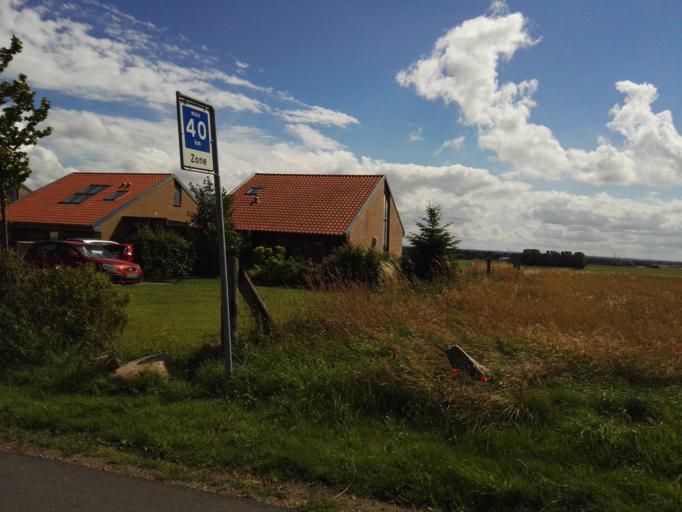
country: DK
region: Capital Region
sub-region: Egedal Kommune
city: Stenlose
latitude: 55.8025
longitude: 12.2142
